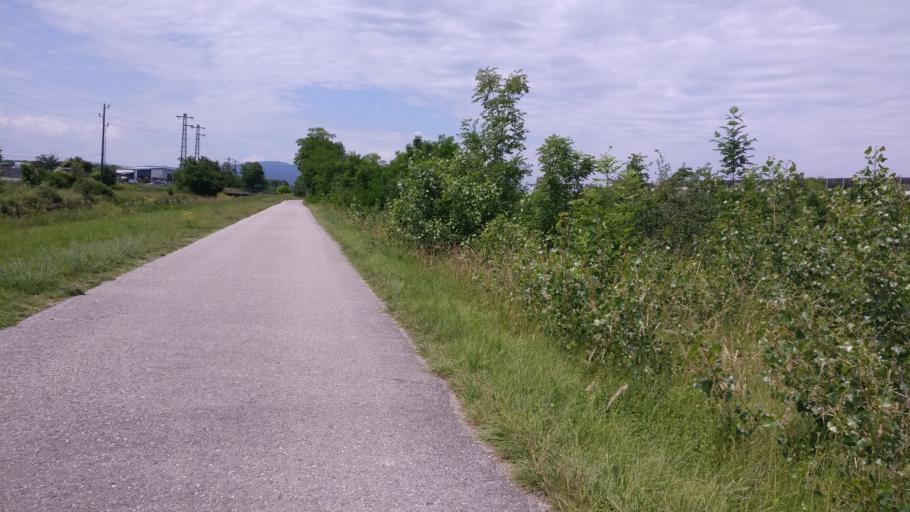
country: AT
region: Lower Austria
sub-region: Politischer Bezirk Baden
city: Schonau an der Triesting
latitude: 47.9123
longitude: 16.2595
